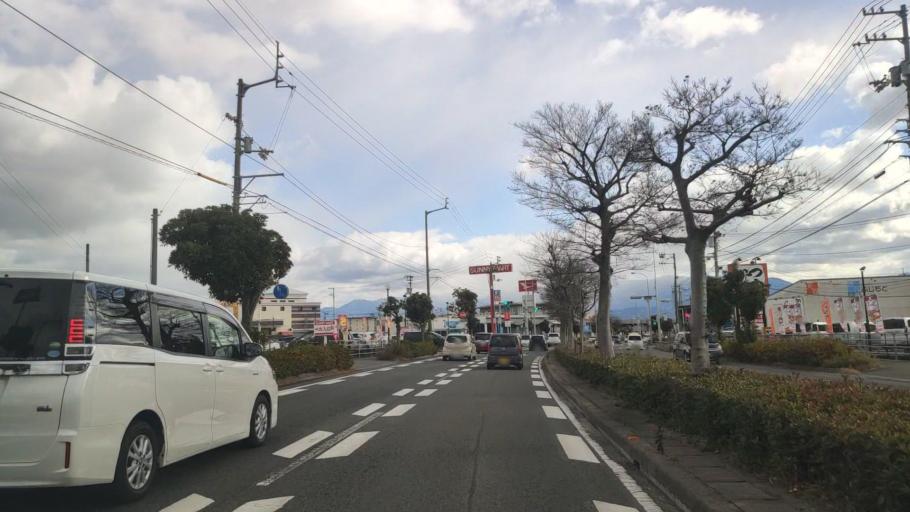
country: JP
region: Ehime
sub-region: Shikoku-chuo Shi
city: Matsuyama
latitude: 33.8187
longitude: 132.7922
